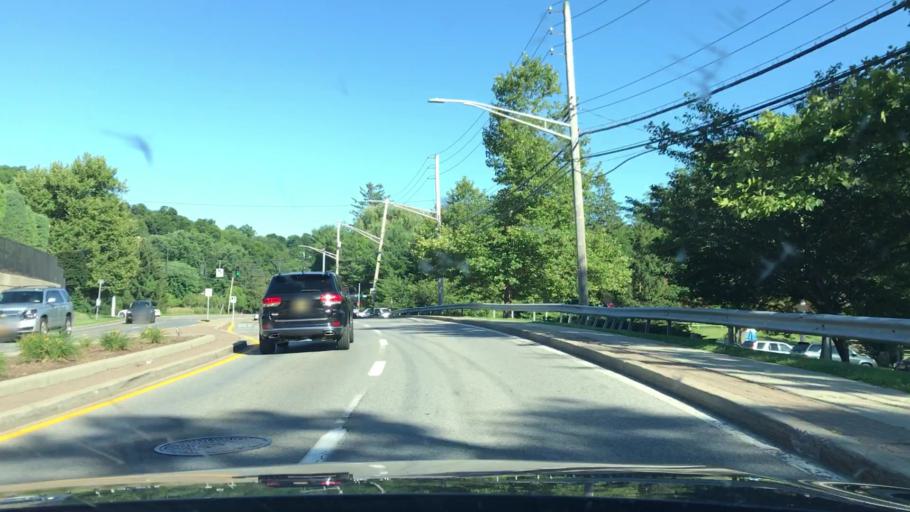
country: US
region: New York
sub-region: Westchester County
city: Thornwood
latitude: 41.1189
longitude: -73.7743
